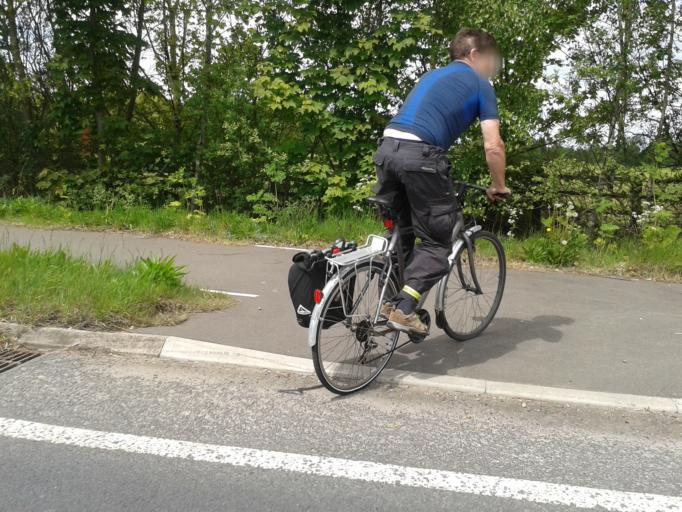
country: GB
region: England
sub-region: Cambridgeshire
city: Meldreth
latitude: 52.1035
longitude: 0.0395
